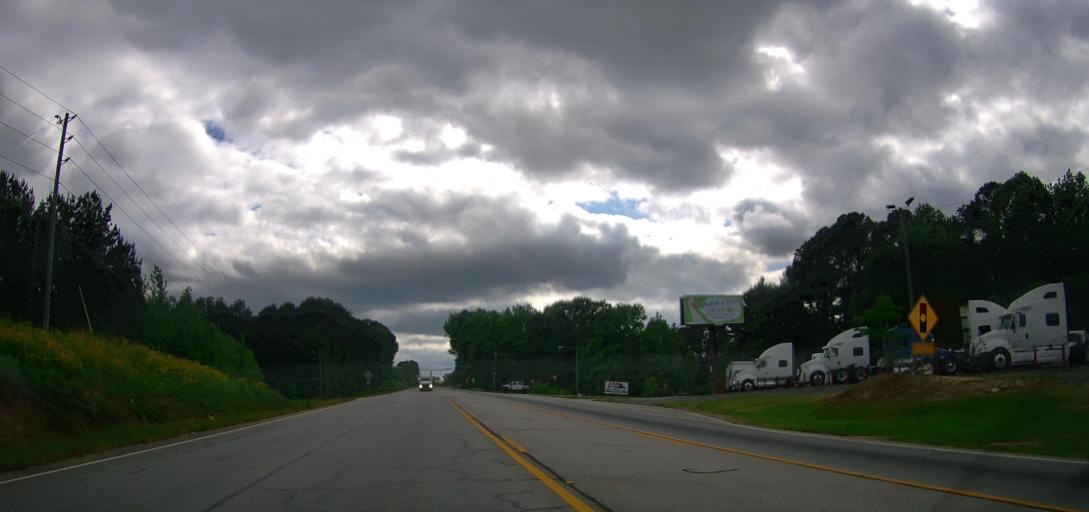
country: US
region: Georgia
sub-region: Walton County
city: Walnut Grove
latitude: 33.7608
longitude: -83.8149
